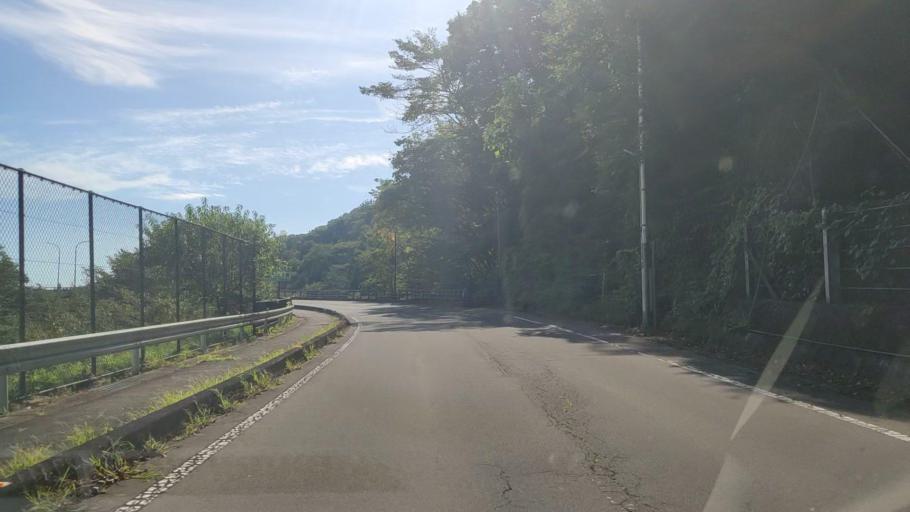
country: JP
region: Gunma
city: Nakanojomachi
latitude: 36.6199
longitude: 138.7643
